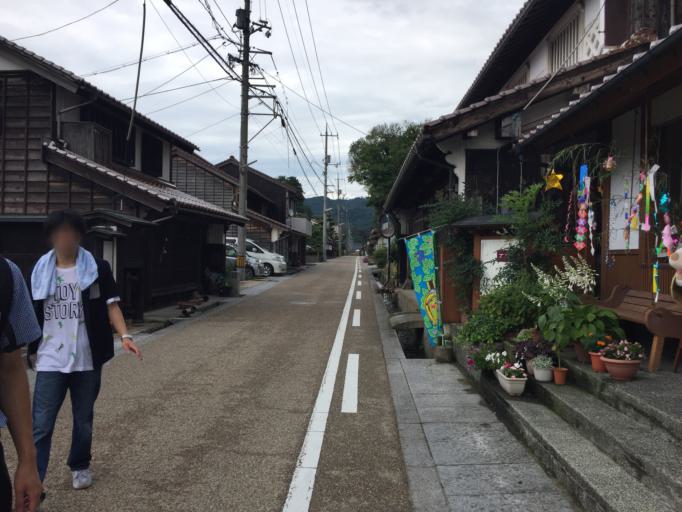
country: JP
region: Tottori
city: Tottori
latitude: 35.4621
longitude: 134.0625
